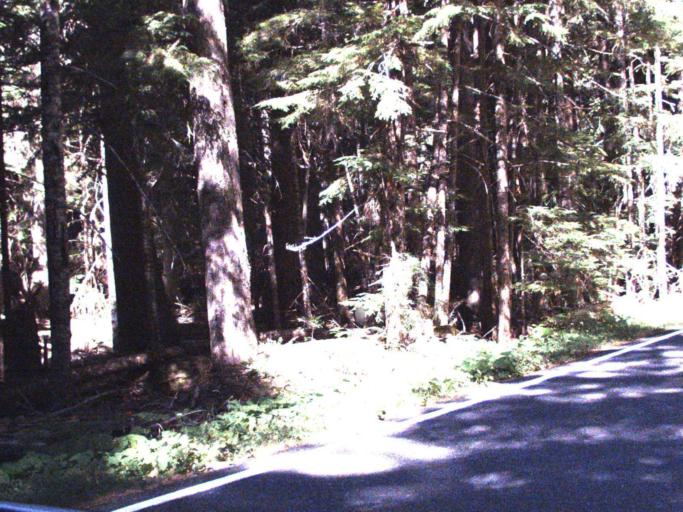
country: US
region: Washington
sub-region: King County
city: Enumclaw
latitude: 46.9716
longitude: -121.5341
